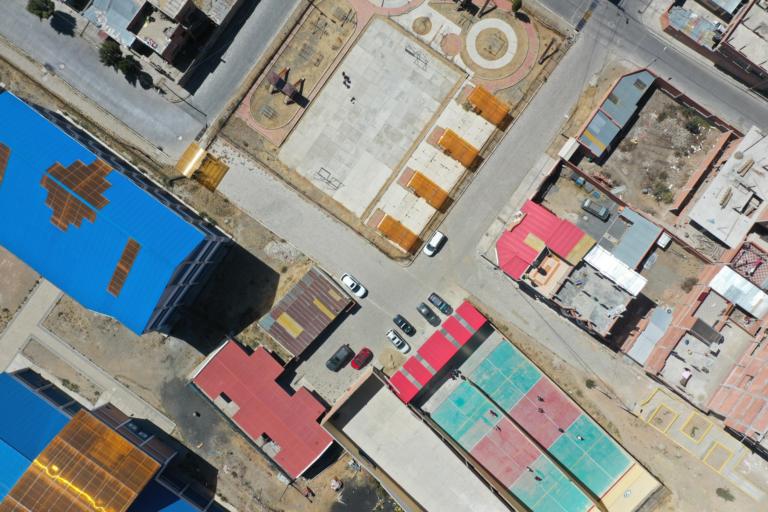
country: BO
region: La Paz
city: La Paz
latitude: -16.5335
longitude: -68.1538
